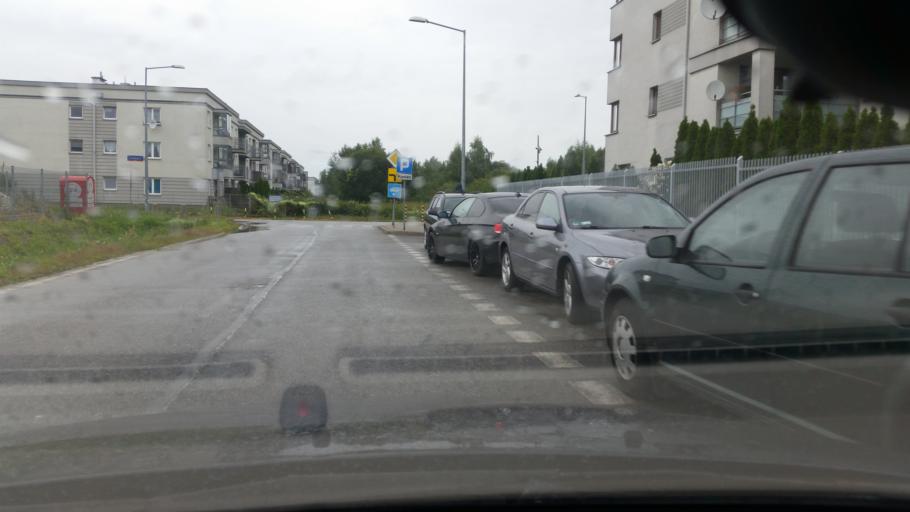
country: PL
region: Masovian Voivodeship
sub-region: Powiat wolominski
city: Marki
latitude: 52.3106
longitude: 21.0805
